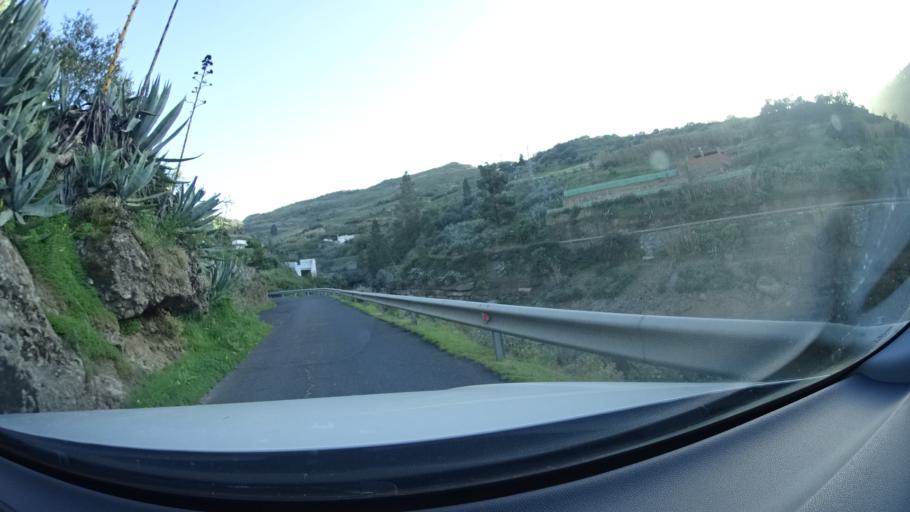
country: ES
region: Canary Islands
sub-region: Provincia de Las Palmas
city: Artenara
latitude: 28.0442
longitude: -15.6711
